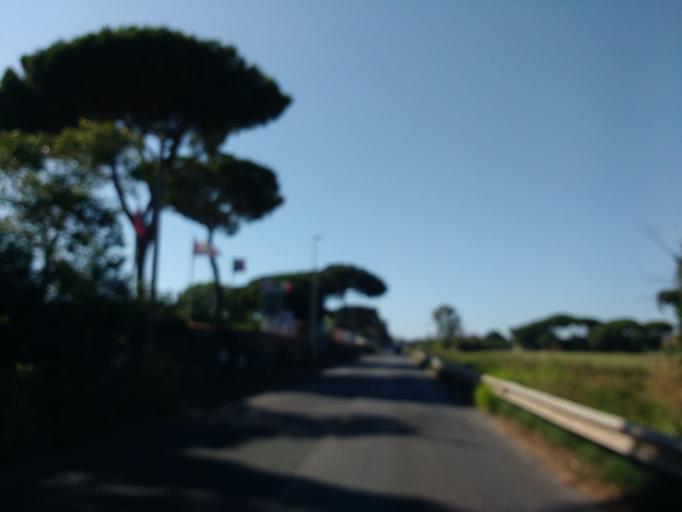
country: IT
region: Latium
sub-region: Citta metropolitana di Roma Capitale
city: Acilia-Castel Fusano-Ostia Antica
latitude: 41.7431
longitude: 12.3383
